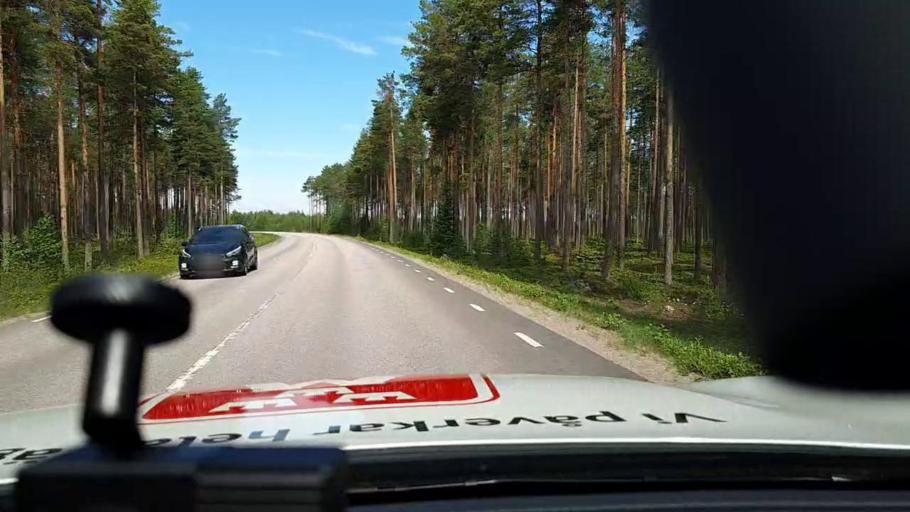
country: SE
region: Norrbotten
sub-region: Lulea Kommun
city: Sodra Sunderbyn
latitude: 65.6316
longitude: 21.9243
